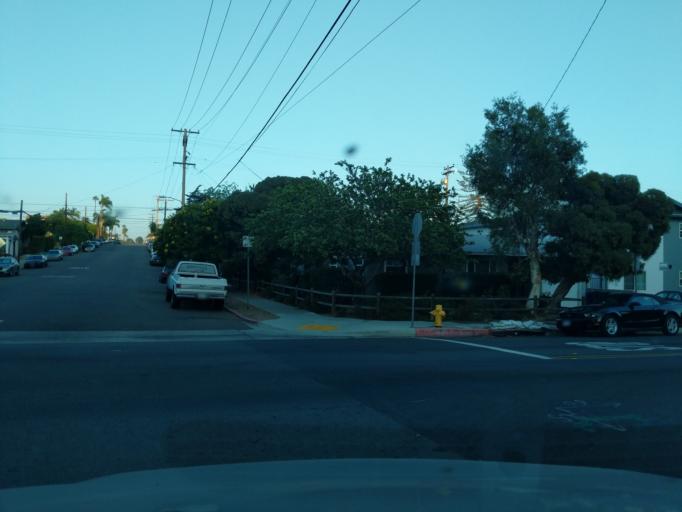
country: US
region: California
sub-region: San Diego County
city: San Diego
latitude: 32.7521
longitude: -117.1439
